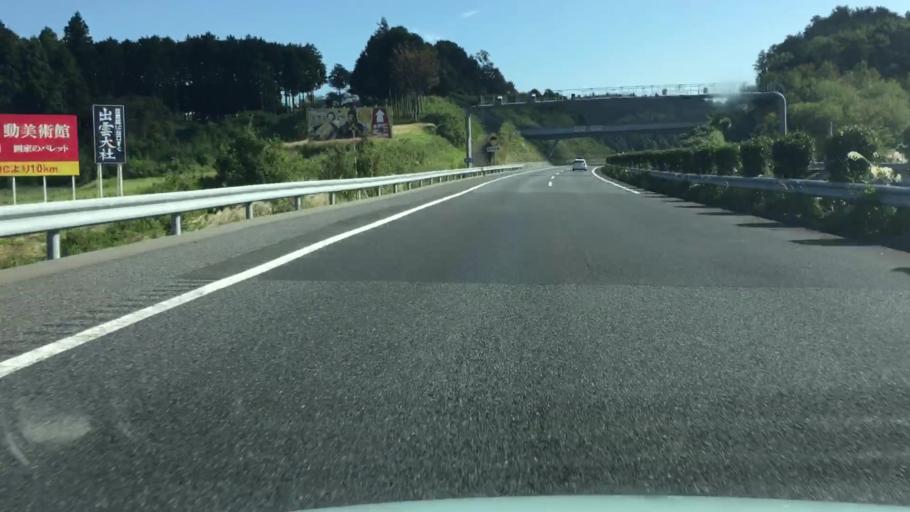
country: JP
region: Ibaraki
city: Iwase
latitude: 36.3472
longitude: 140.1558
